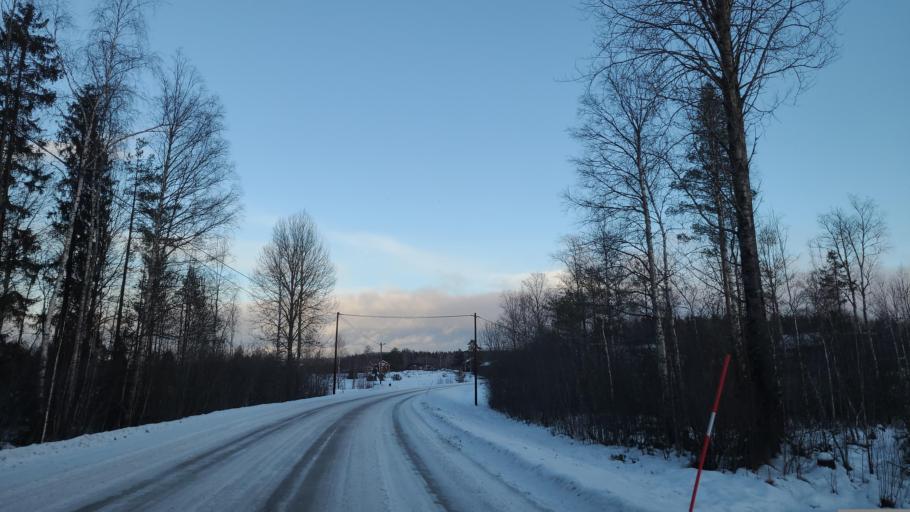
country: SE
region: Gaevleborg
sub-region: Bollnas Kommun
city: Bollnas
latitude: 61.3879
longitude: 16.4022
